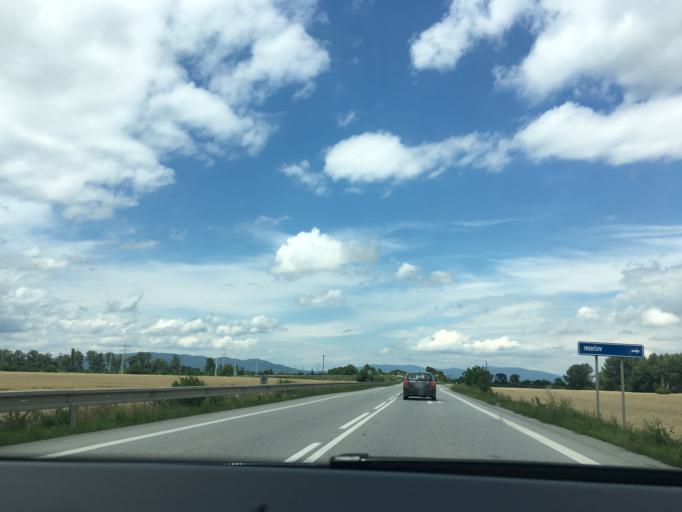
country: SK
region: Kosicky
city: Trebisov
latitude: 48.6211
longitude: 21.7015
